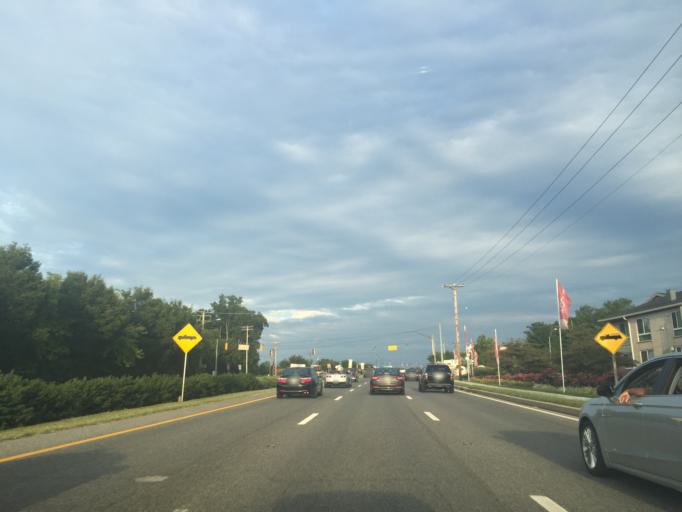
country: US
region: Maryland
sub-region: Anne Arundel County
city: Maryland City
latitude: 39.1008
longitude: -76.8206
